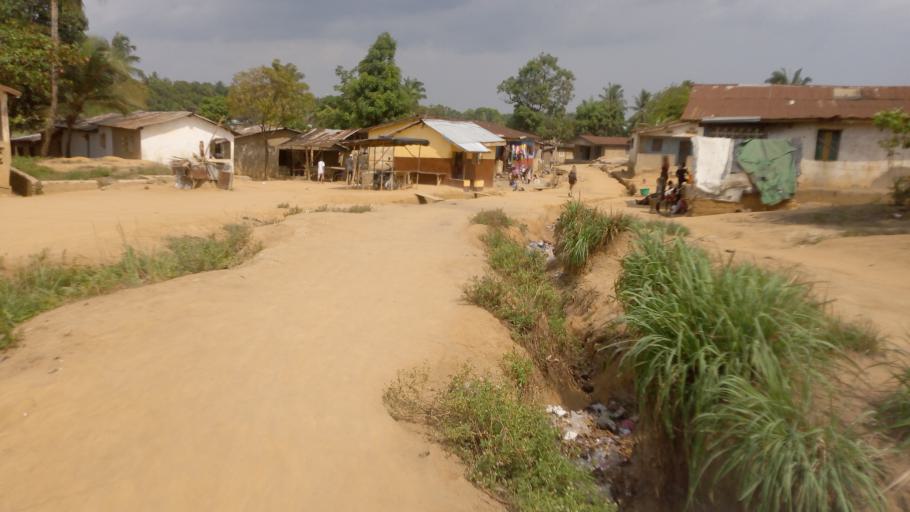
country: SL
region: Western Area
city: Waterloo
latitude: 8.3242
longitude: -13.0613
